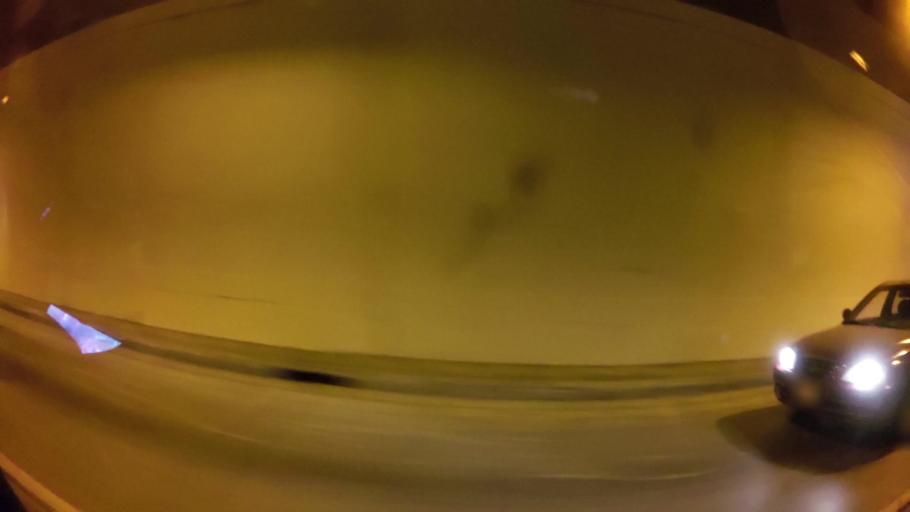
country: EC
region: Guayas
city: Eloy Alfaro
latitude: -2.1807
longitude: -79.8803
